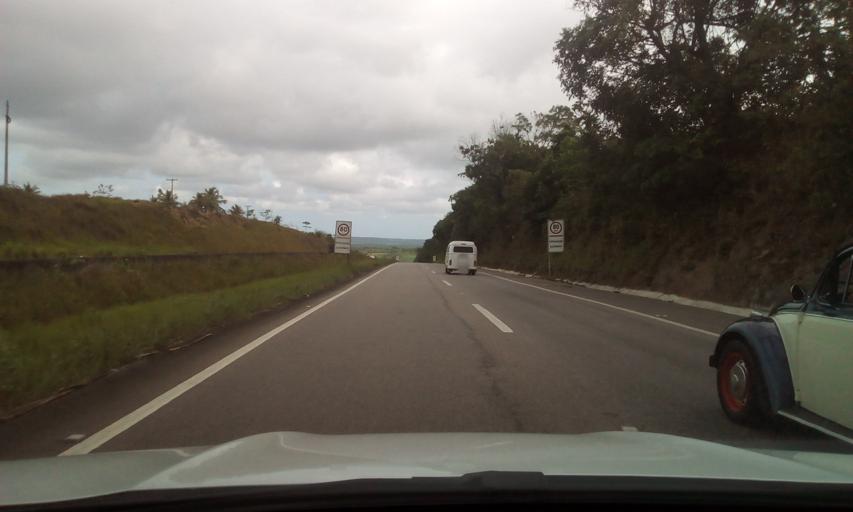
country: BR
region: Pernambuco
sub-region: Itapissuma
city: Itapissuma
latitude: -7.6787
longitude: -34.9270
